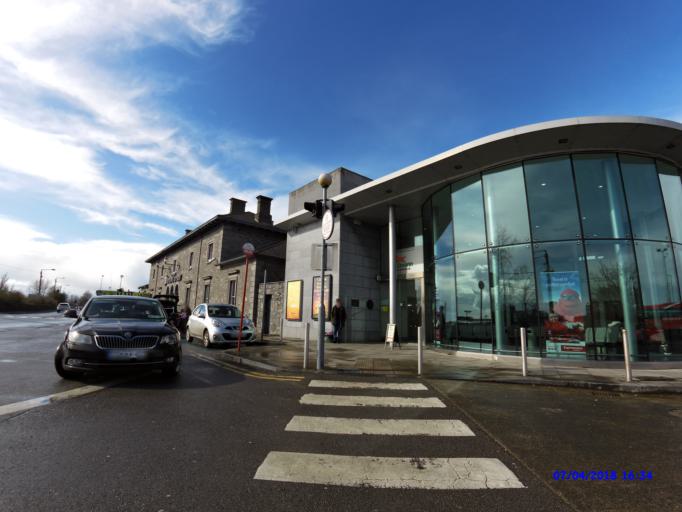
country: IE
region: Leinster
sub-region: An Iarmhi
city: Athlone
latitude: 53.4266
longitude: -7.9353
